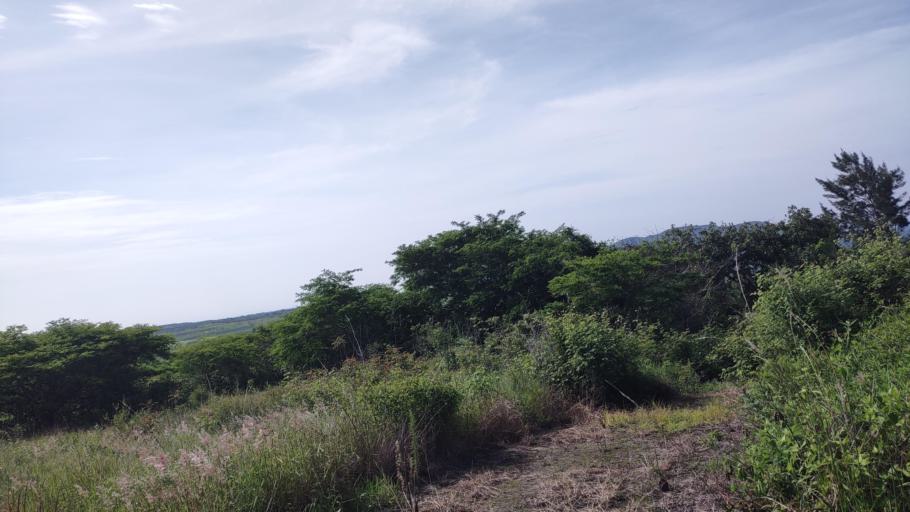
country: MX
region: Veracruz
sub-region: Emiliano Zapata
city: Dos Rios
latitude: 19.4706
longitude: -96.8227
